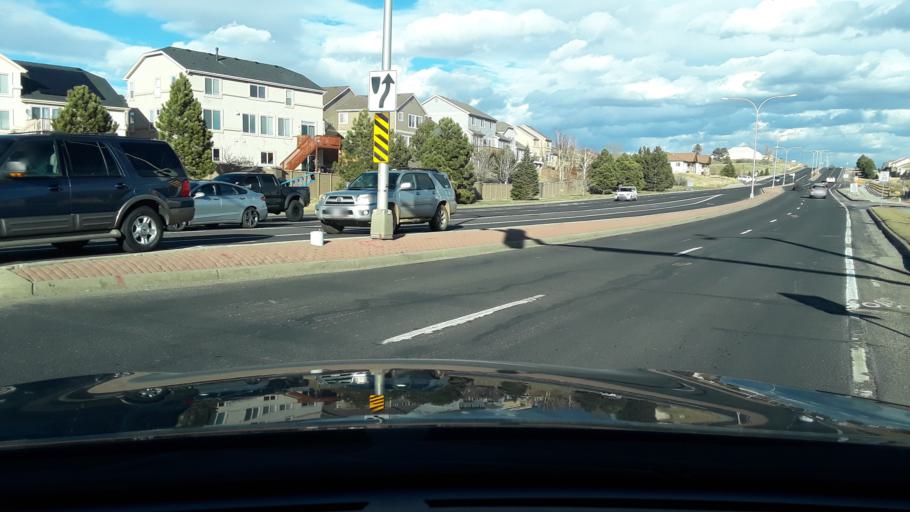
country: US
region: Colorado
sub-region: El Paso County
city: Gleneagle
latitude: 39.0271
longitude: -104.8169
